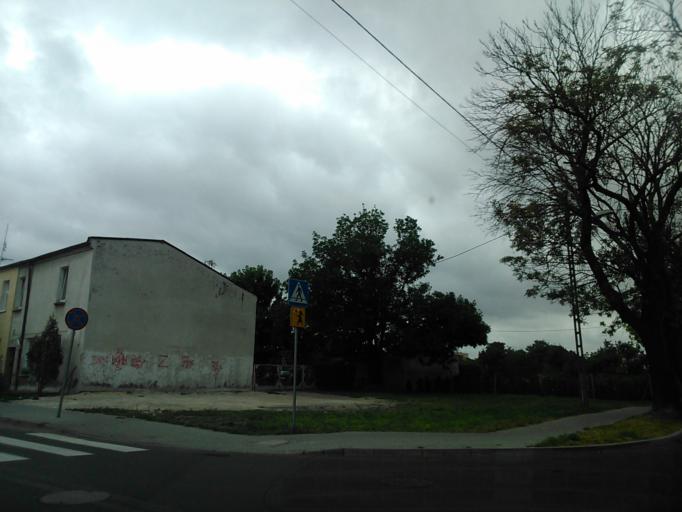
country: PL
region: Kujawsko-Pomorskie
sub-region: Powiat inowroclawski
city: Inowroclaw
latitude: 52.7970
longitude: 18.2819
